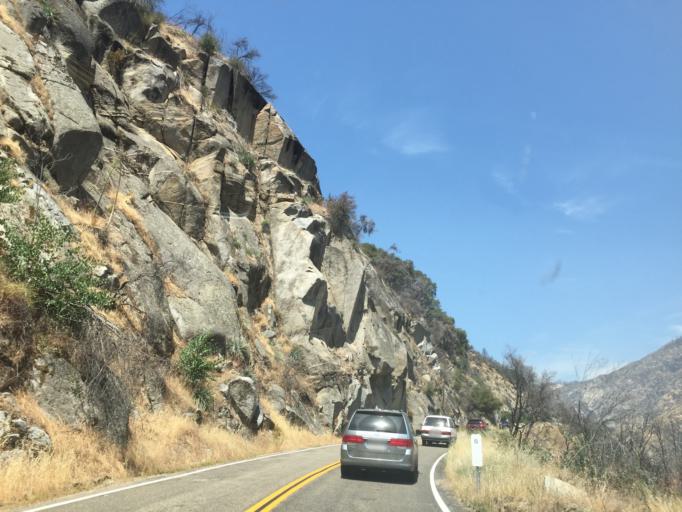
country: US
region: California
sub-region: Fresno County
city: Squaw Valley
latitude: 36.8293
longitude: -118.8714
